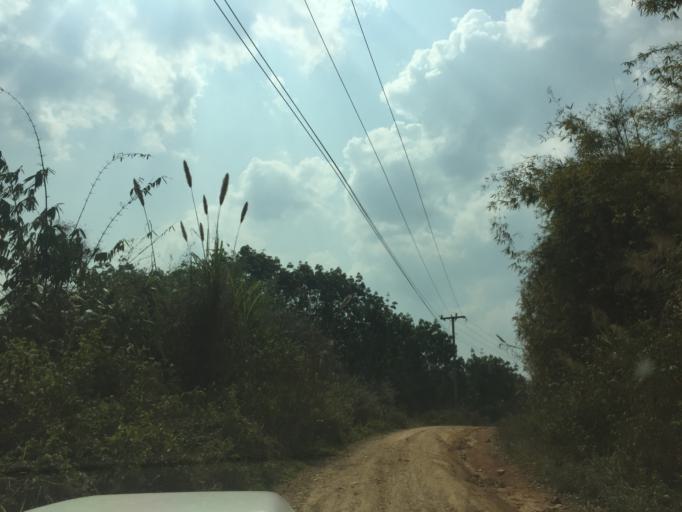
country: TH
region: Nan
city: Thung Chang
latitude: 19.7316
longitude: 100.7357
